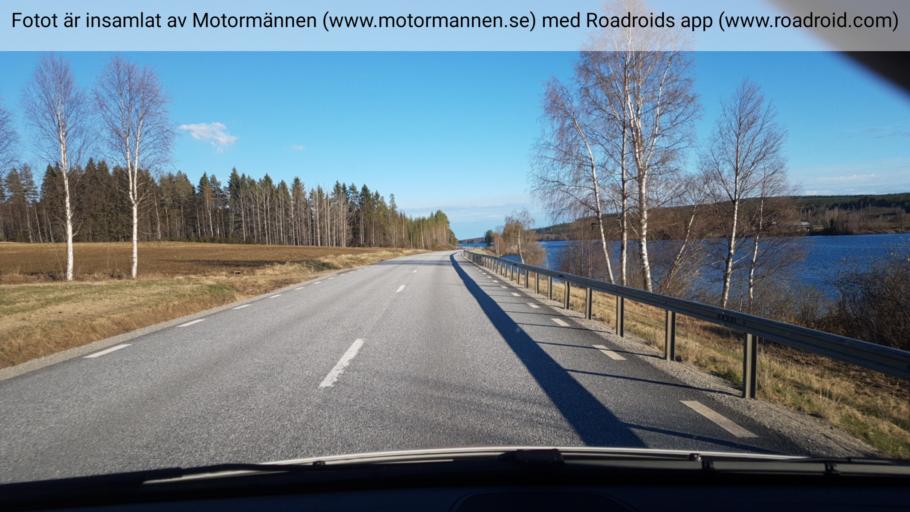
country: SE
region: Vaesterbotten
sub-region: Vindelns Kommun
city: Vindeln
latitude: 64.1820
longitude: 19.4755
